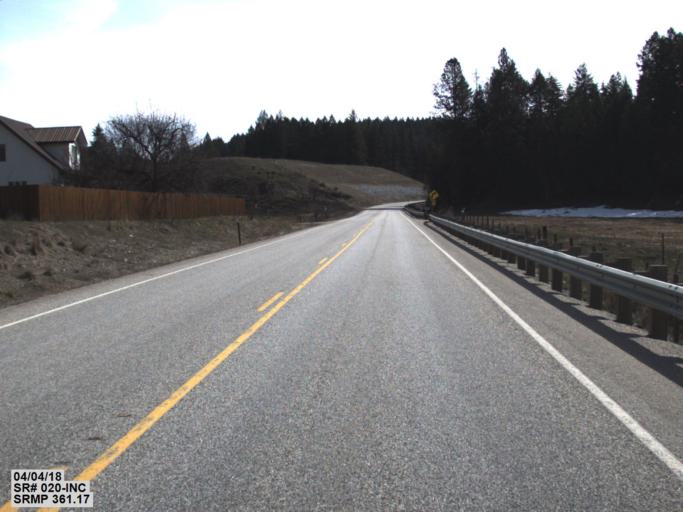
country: US
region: Washington
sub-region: Stevens County
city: Colville
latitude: 48.5151
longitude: -117.7845
